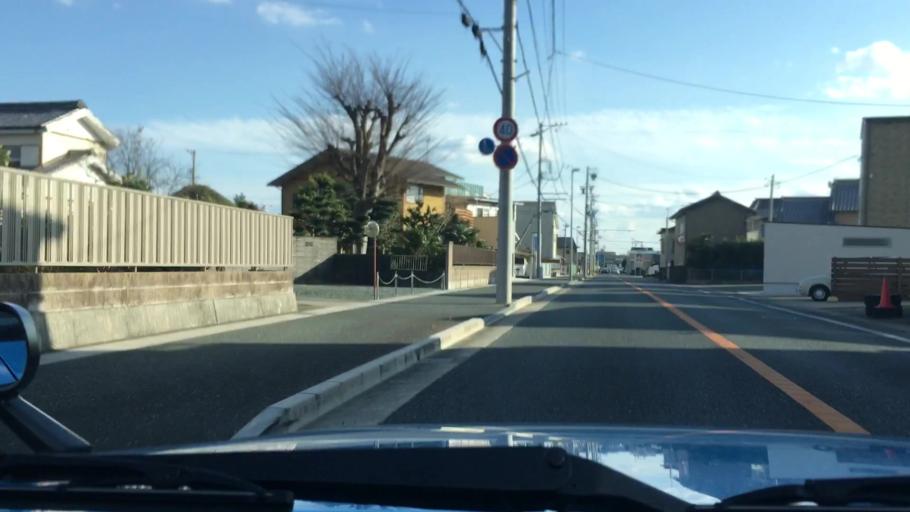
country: JP
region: Shizuoka
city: Hamamatsu
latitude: 34.7550
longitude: 137.6703
